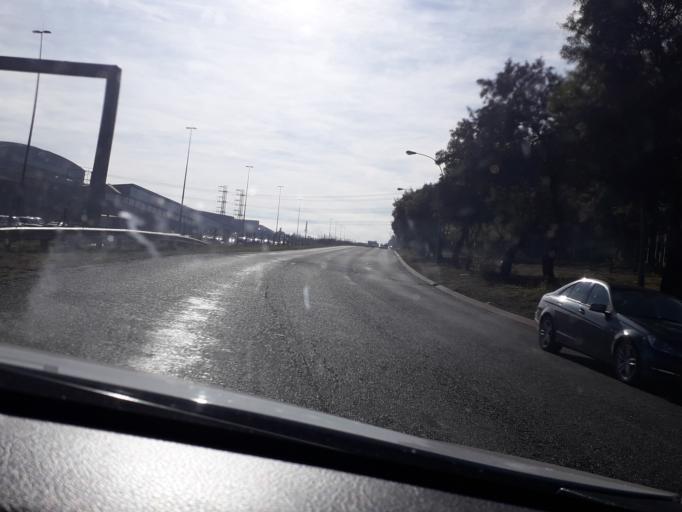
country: ZA
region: Gauteng
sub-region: Ekurhuleni Metropolitan Municipality
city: Germiston
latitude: -26.1645
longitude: 28.1748
